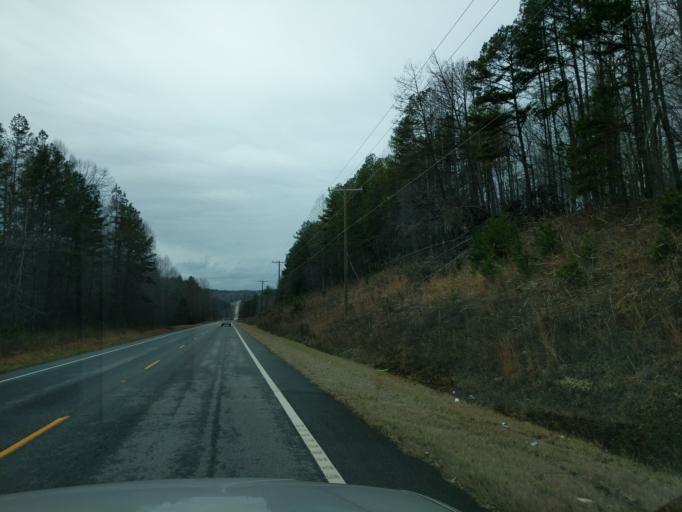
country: US
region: South Carolina
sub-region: Pickens County
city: Pickens
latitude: 34.9265
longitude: -82.8945
